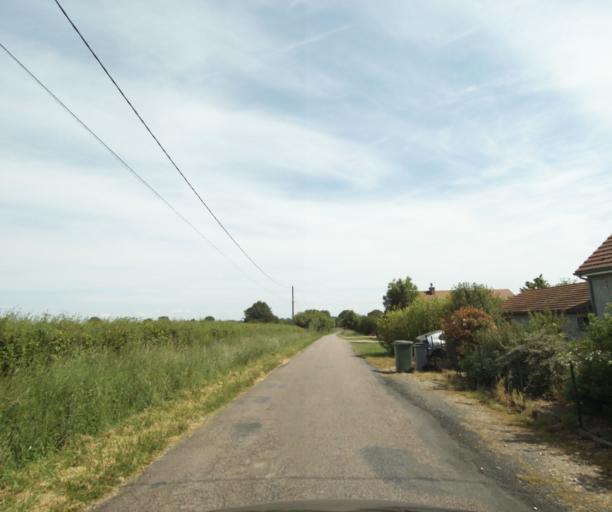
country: FR
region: Bourgogne
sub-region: Departement de Saone-et-Loire
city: Palinges
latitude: 46.5498
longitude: 4.1771
